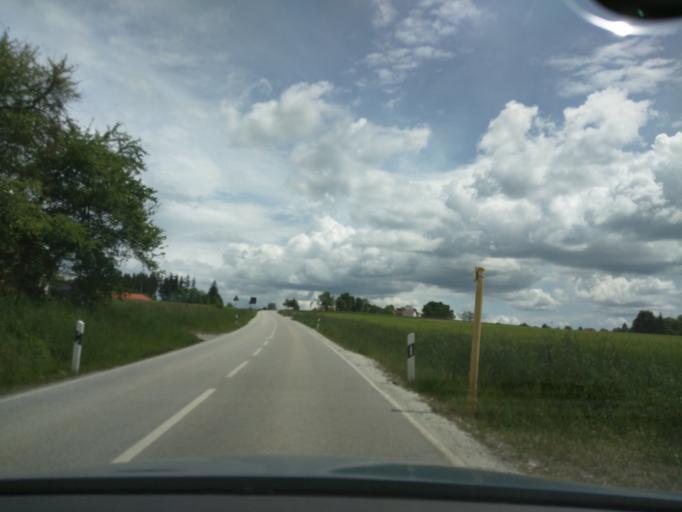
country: DE
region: Bavaria
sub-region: Lower Bavaria
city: Furstenzell
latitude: 48.5304
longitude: 13.3479
